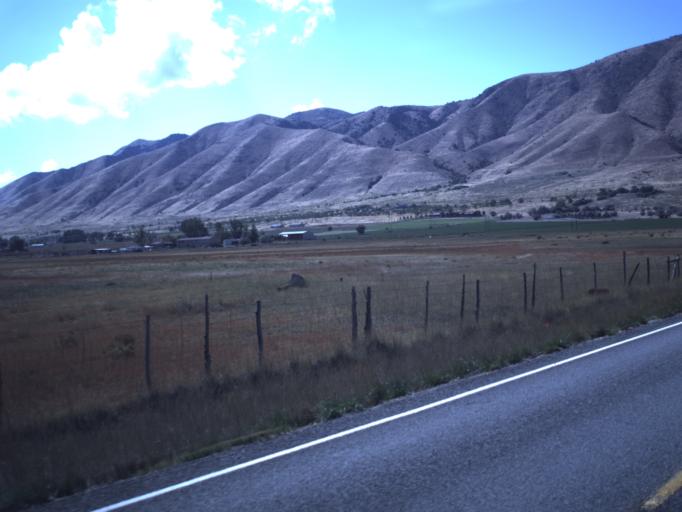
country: US
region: Utah
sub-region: Utah County
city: West Mountain
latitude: 40.0979
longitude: -111.7808
